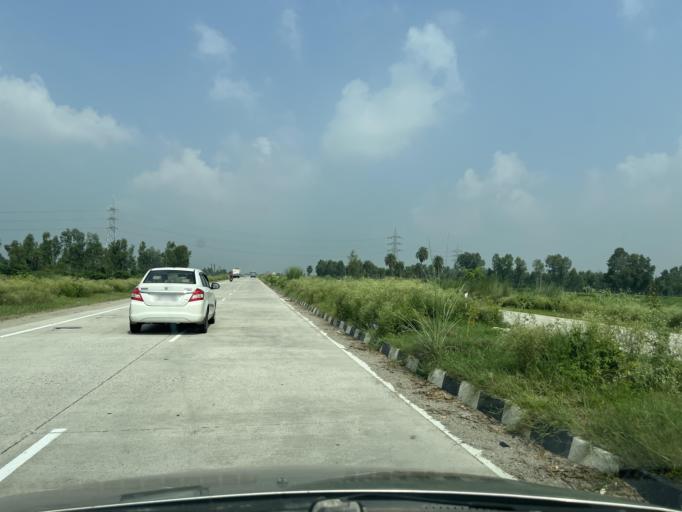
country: IN
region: Uttarakhand
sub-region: Udham Singh Nagar
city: Kashipur
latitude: 29.1651
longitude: 78.9596
